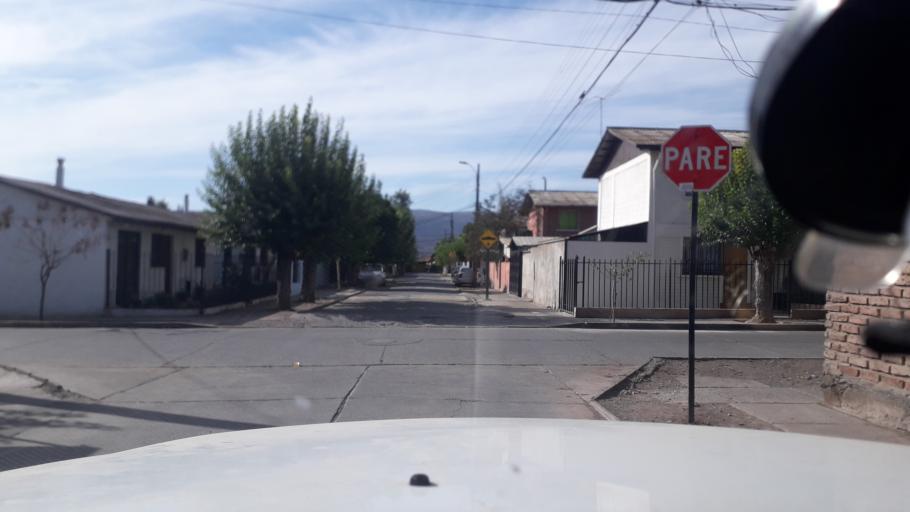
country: CL
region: Valparaiso
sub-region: Provincia de San Felipe
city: San Felipe
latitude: -32.7501
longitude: -70.7158
